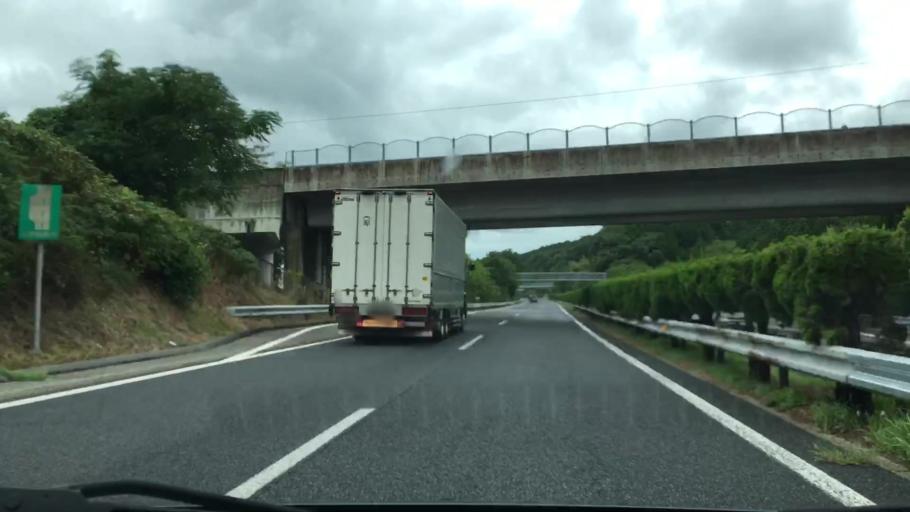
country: JP
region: Okayama
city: Tsuyama
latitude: 35.0371
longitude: 134.1321
